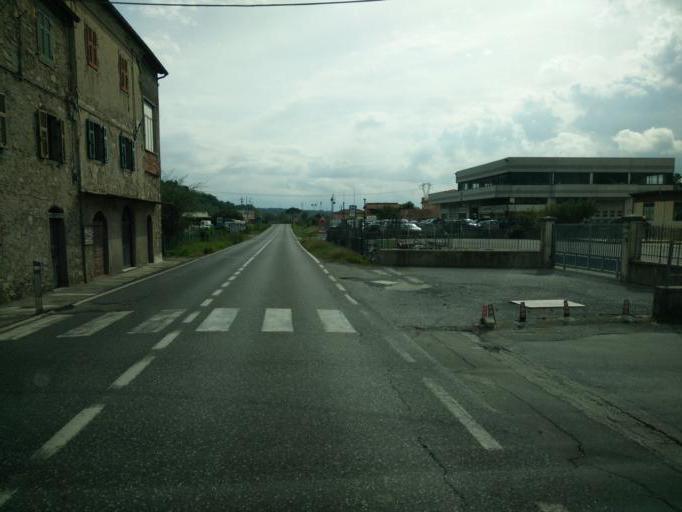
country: IT
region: Tuscany
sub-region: Provincia di Massa-Carrara
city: Pontremoli
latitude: 44.3597
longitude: 9.9003
